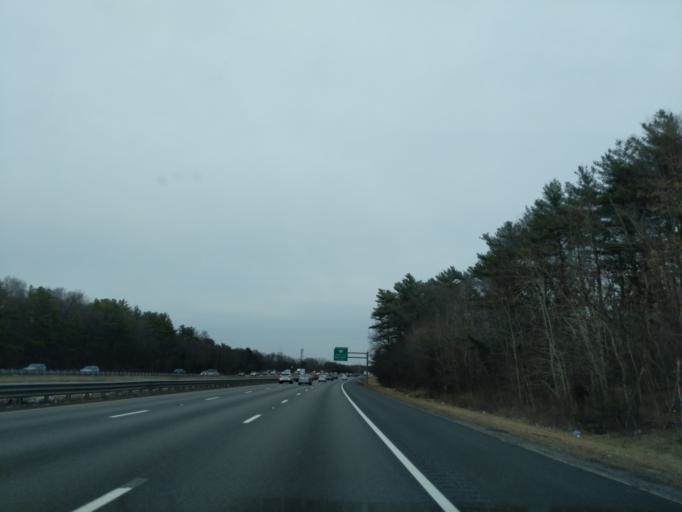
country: US
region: Massachusetts
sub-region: Norfolk County
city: Plainville
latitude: 41.9977
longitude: -71.2910
